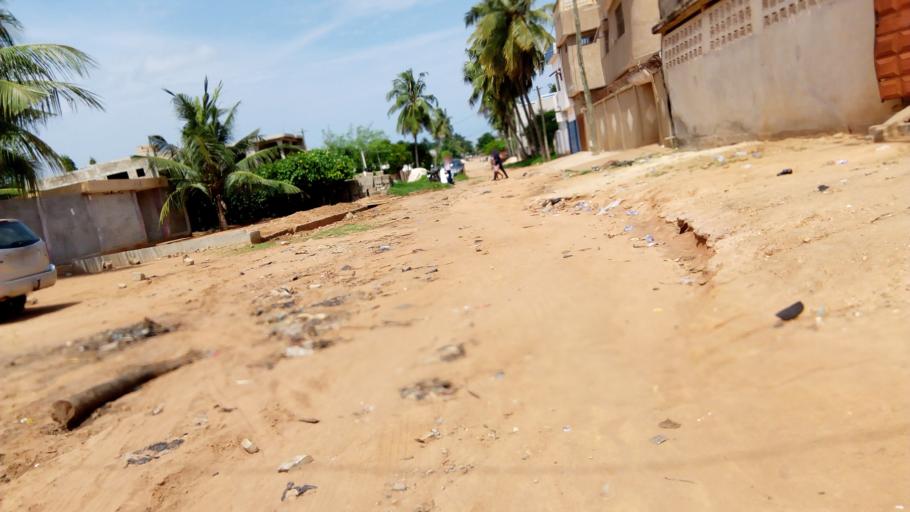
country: TG
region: Maritime
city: Lome
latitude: 6.1819
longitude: 1.1715
